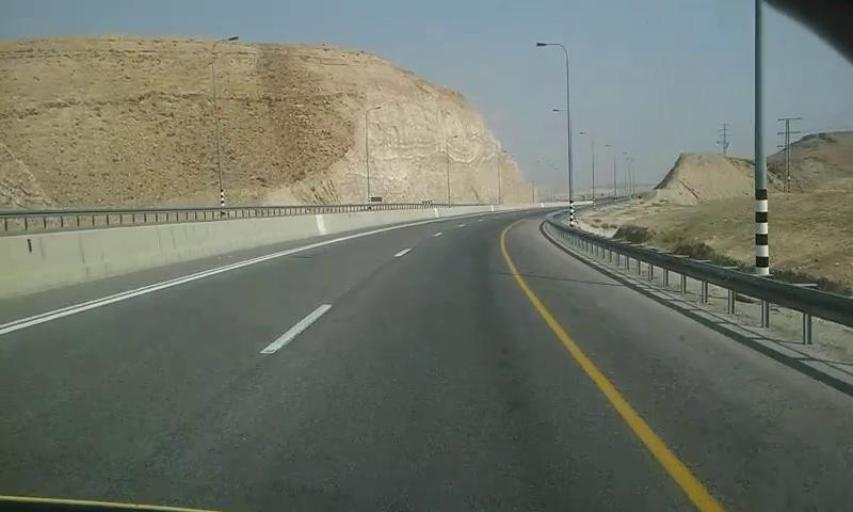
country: PS
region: West Bank
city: Jericho
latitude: 31.7999
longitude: 35.4404
